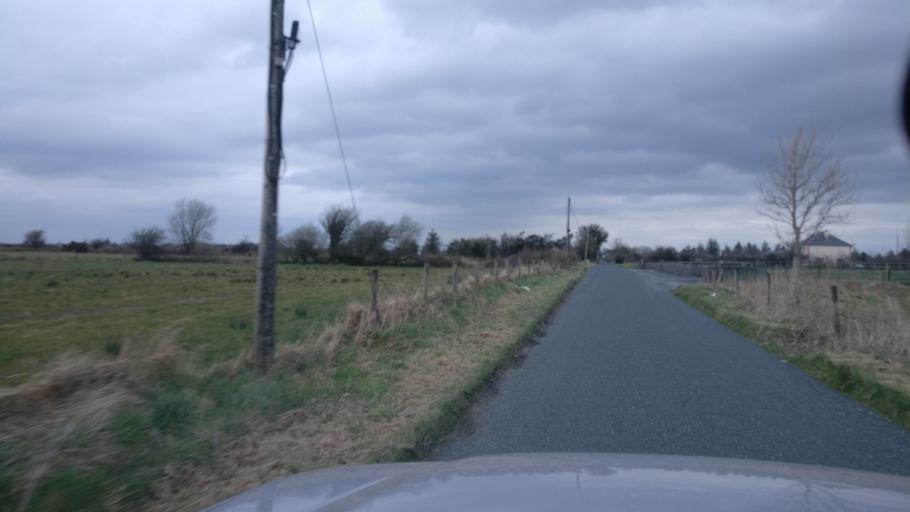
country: IE
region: Connaught
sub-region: County Galway
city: Loughrea
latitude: 53.2419
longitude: -8.5192
